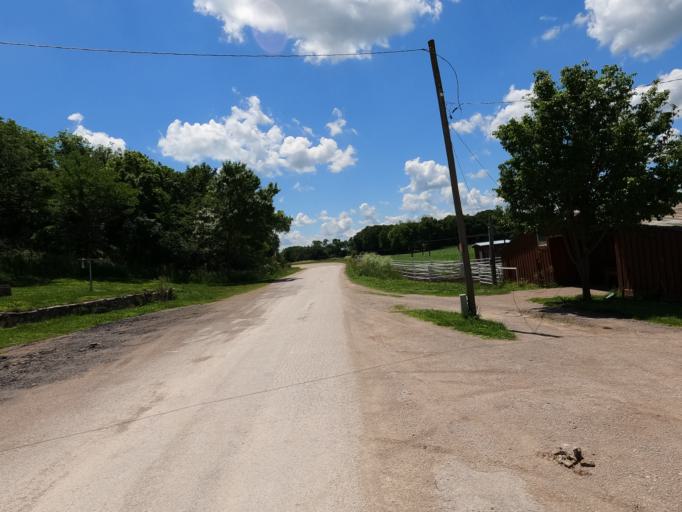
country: US
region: Kansas
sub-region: Marion County
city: Marion
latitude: 38.2420
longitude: -96.8066
